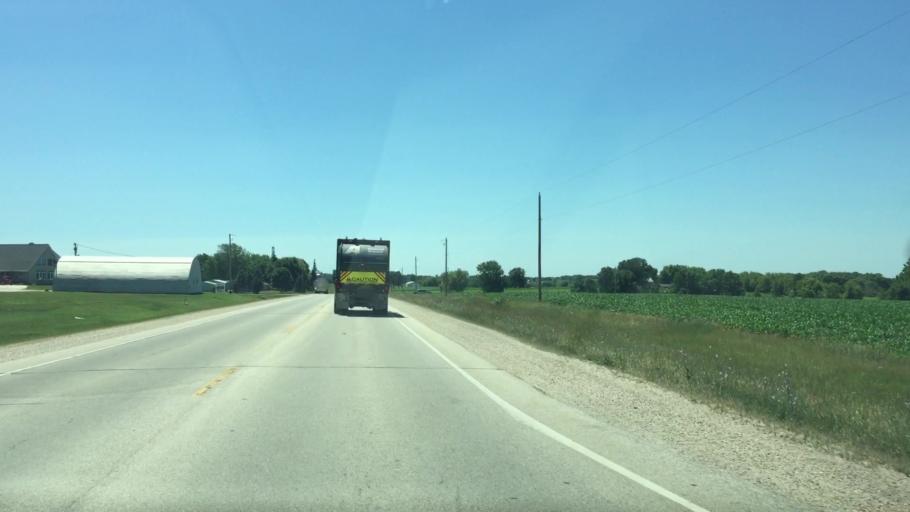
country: US
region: Wisconsin
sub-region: Calumet County
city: Hilbert
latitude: 44.0872
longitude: -88.1636
